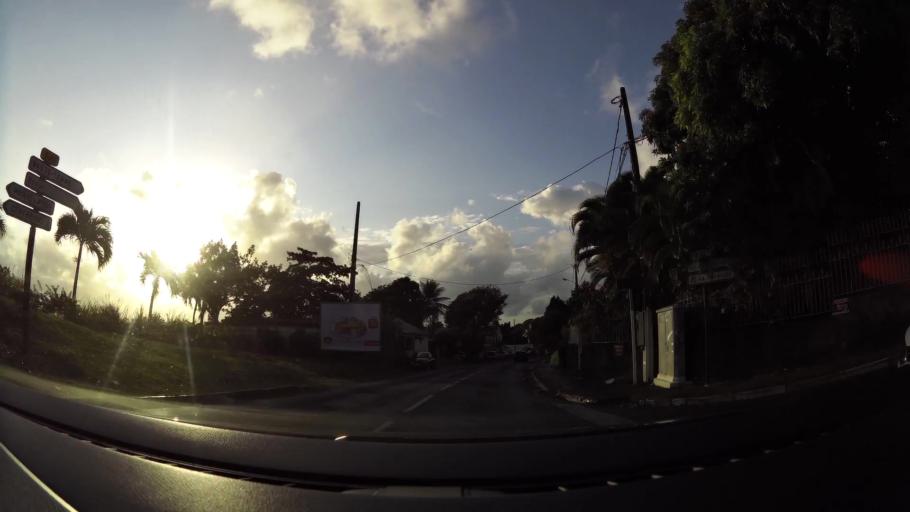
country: GP
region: Guadeloupe
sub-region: Guadeloupe
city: Petit-Bourg
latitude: 16.1884
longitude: -61.5901
